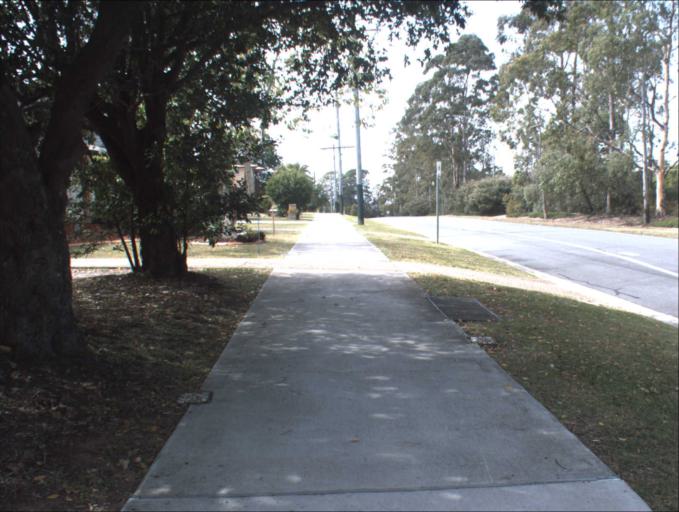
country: AU
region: Queensland
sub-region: Logan
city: Springwood
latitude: -27.6222
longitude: 153.1456
